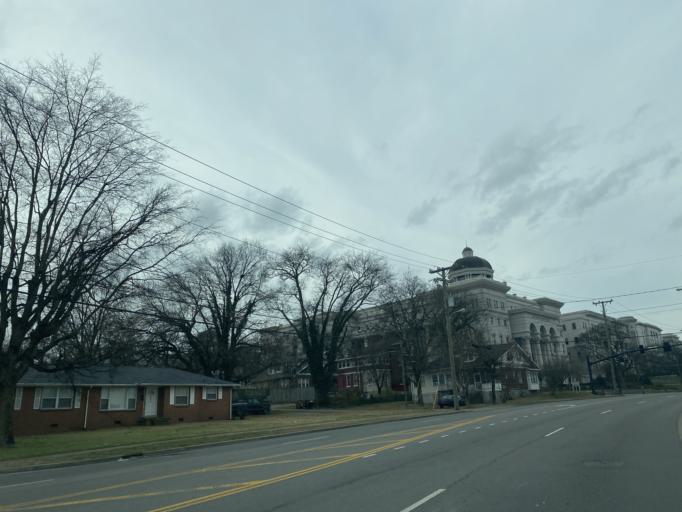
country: US
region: Tennessee
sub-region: Davidson County
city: Nashville
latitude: 36.1360
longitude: -86.7908
